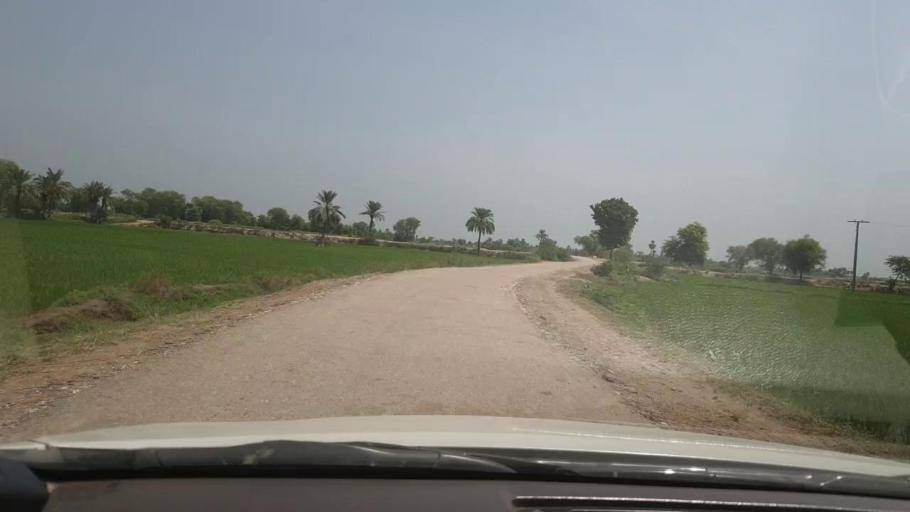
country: PK
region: Sindh
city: Shikarpur
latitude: 27.9416
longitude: 68.5982
